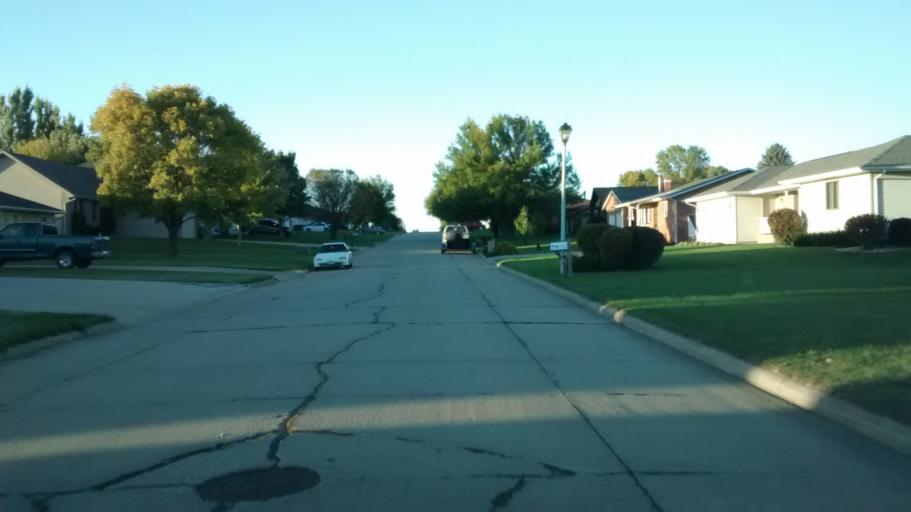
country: US
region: Iowa
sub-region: Woodbury County
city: Moville
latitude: 42.4935
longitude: -96.0666
